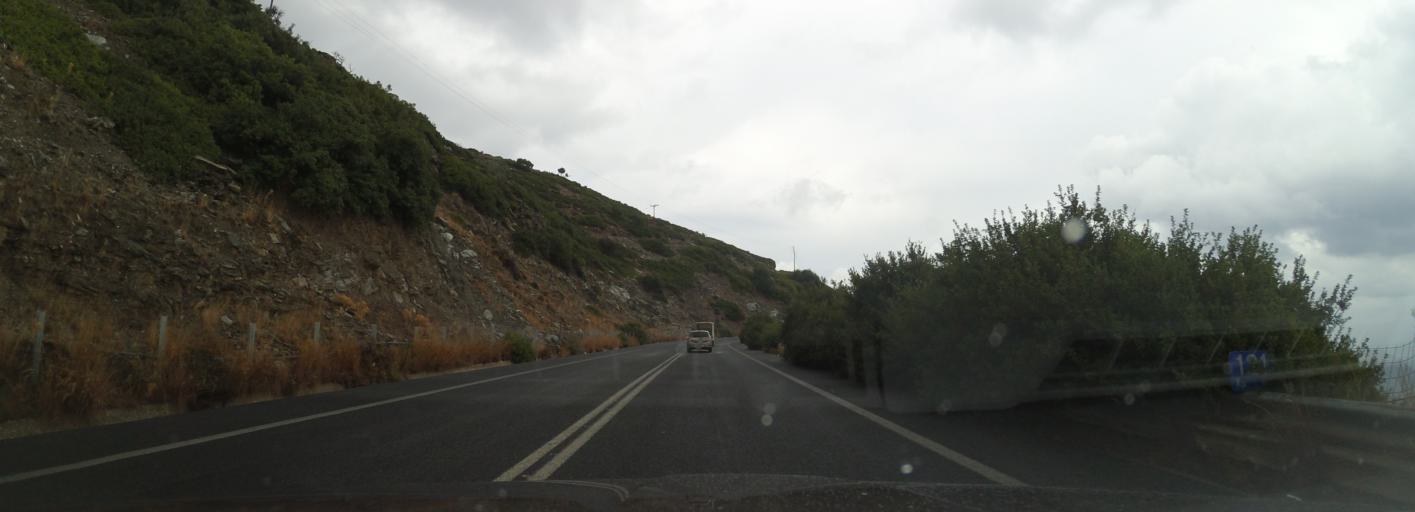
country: GR
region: Crete
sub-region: Nomos Irakleiou
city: Gazi
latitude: 35.3845
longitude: 25.0363
